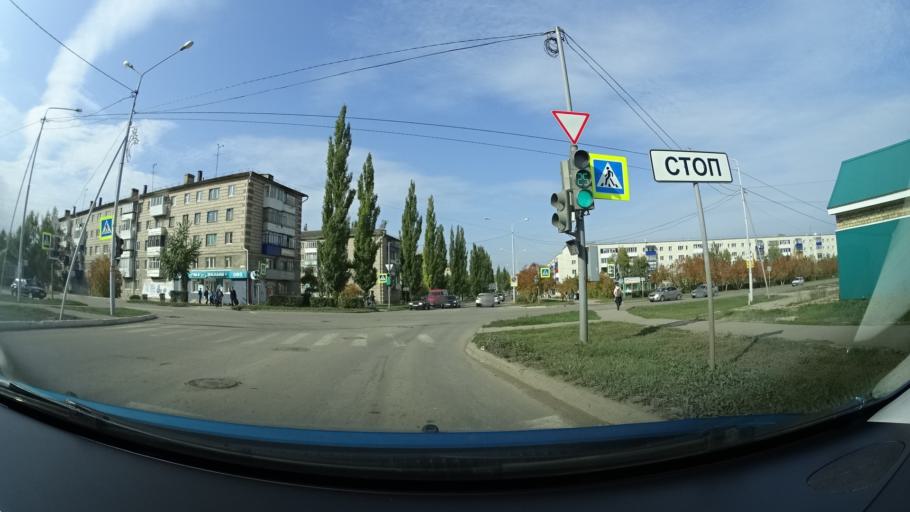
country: RU
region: Bashkortostan
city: Tuymazy
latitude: 54.5985
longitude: 53.7072
